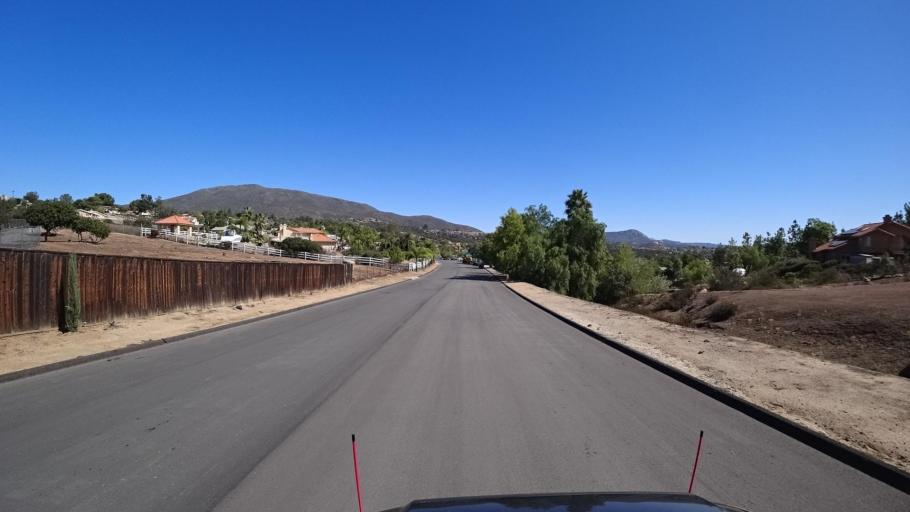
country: US
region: California
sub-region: San Diego County
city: Alpine
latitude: 32.8441
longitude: -116.7663
